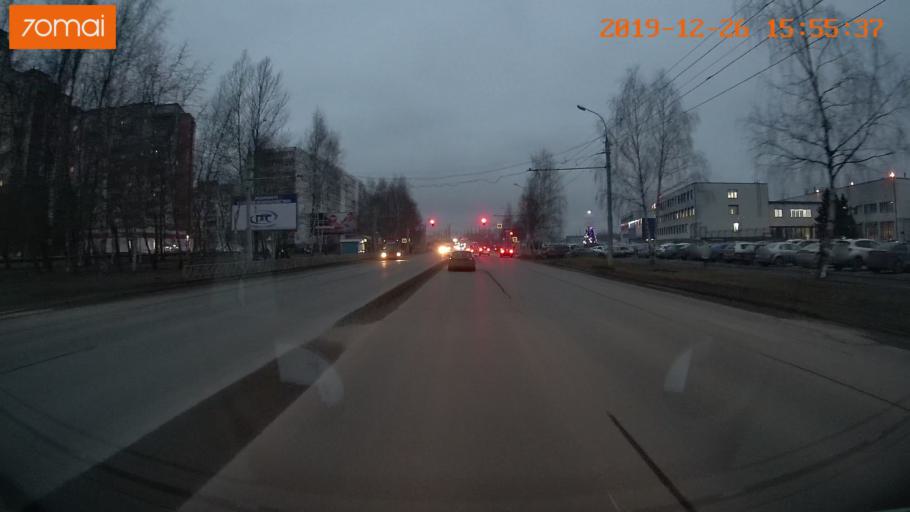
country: RU
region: Jaroslavl
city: Rybinsk
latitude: 58.0432
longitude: 38.8092
